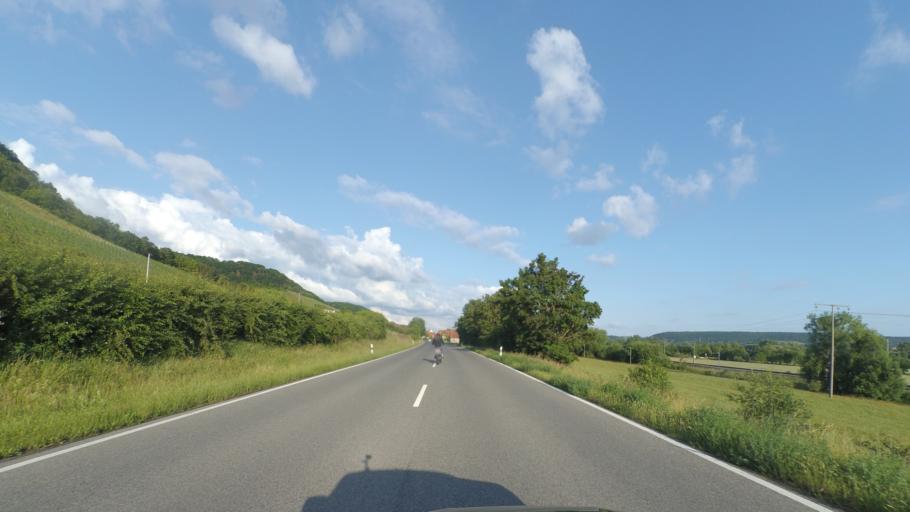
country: DE
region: Bavaria
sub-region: Regierungsbezirk Unterfranken
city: Zeil
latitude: 50.0024
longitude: 10.6099
